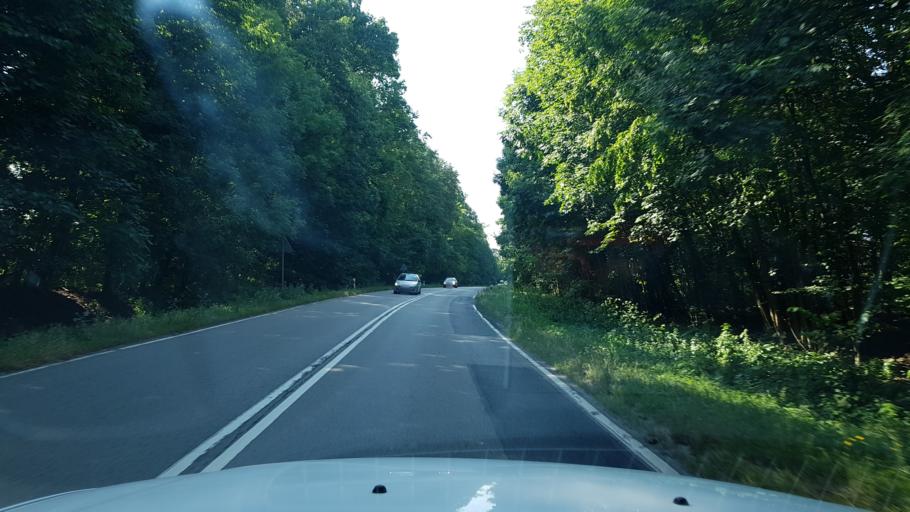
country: PL
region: West Pomeranian Voivodeship
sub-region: Powiat gryfinski
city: Stare Czarnowo
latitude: 53.3357
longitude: 14.7690
